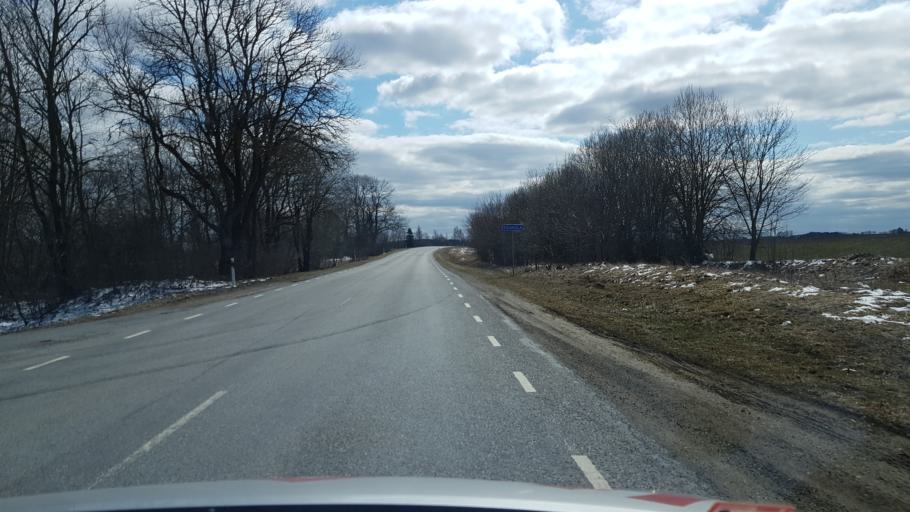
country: EE
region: Laeaene-Virumaa
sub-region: Tapa vald
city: Tapa
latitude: 59.3250
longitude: 26.0027
